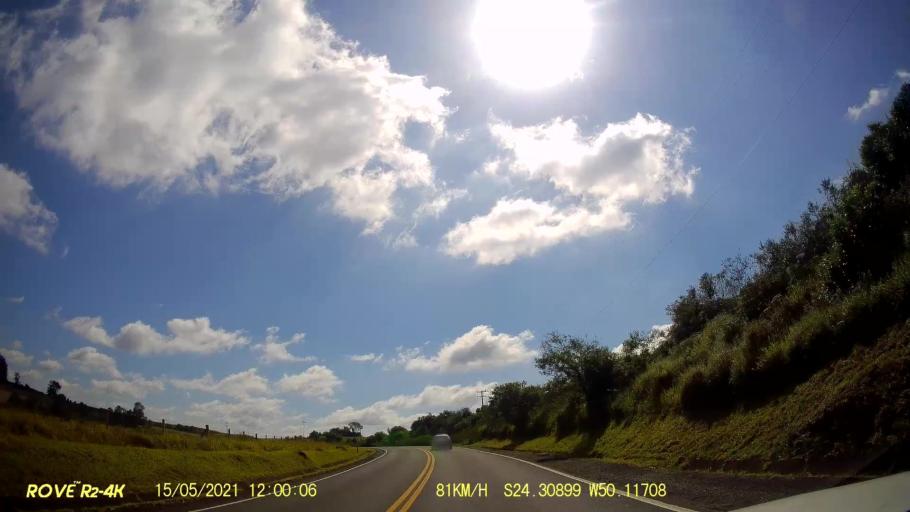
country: BR
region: Parana
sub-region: Pirai Do Sul
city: Pirai do Sul
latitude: -24.3091
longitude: -50.1172
